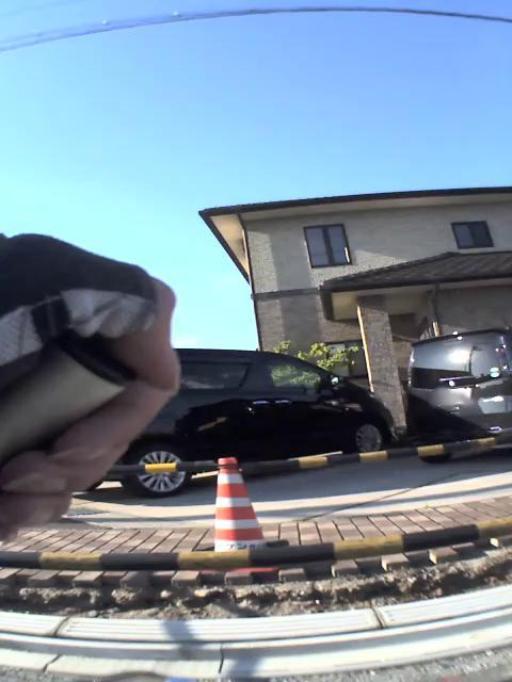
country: JP
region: Yamaguchi
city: Nagato
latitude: 34.3880
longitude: 131.1952
